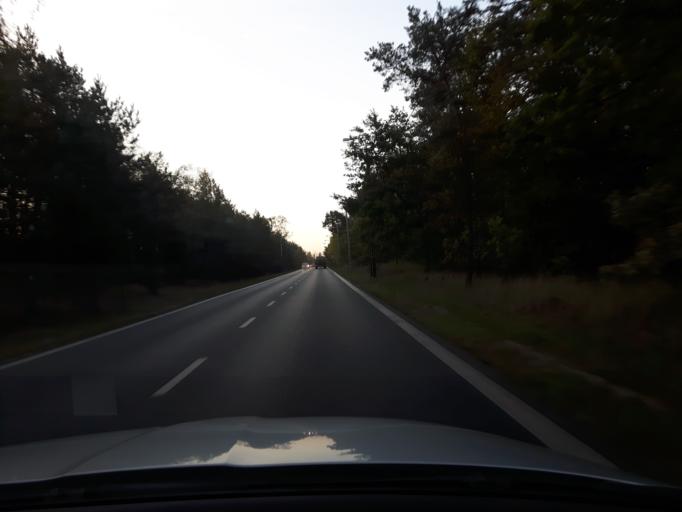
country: PL
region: Masovian Voivodeship
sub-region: Warszawa
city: Wawer
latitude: 52.1973
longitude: 21.1750
